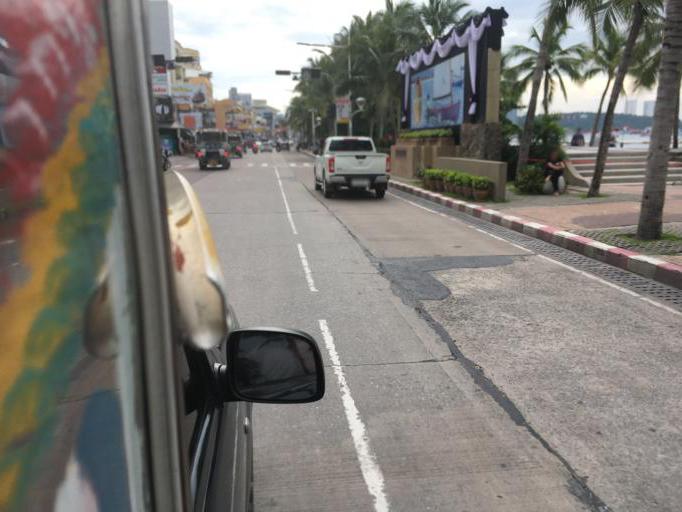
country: TH
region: Chon Buri
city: Phatthaya
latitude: 12.9328
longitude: 100.8803
